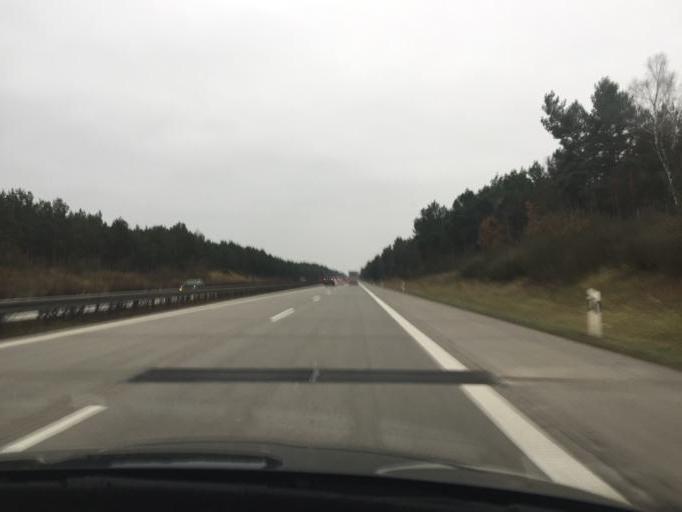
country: DE
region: Brandenburg
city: Teupitz
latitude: 52.1073
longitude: 13.6465
